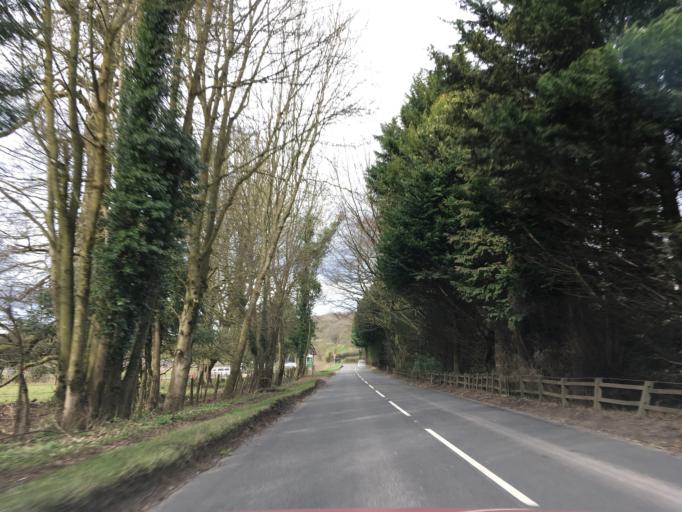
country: GB
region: England
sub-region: Gloucestershire
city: Coleford
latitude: 51.7786
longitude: -2.6098
